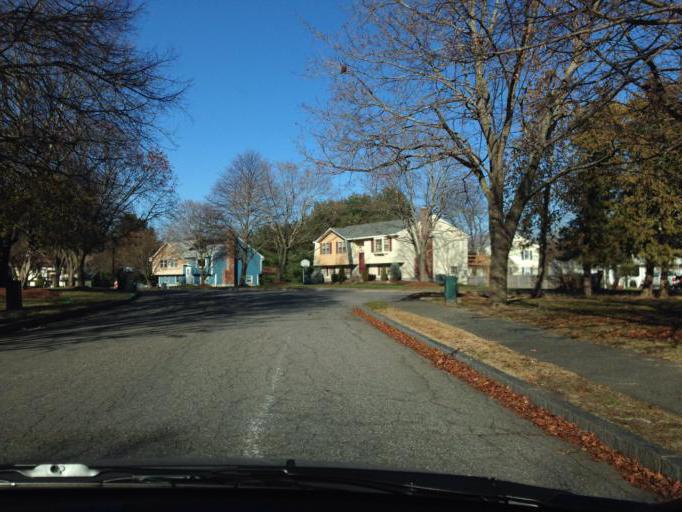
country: US
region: Massachusetts
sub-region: Middlesex County
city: Bedford
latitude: 42.4811
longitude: -71.2823
